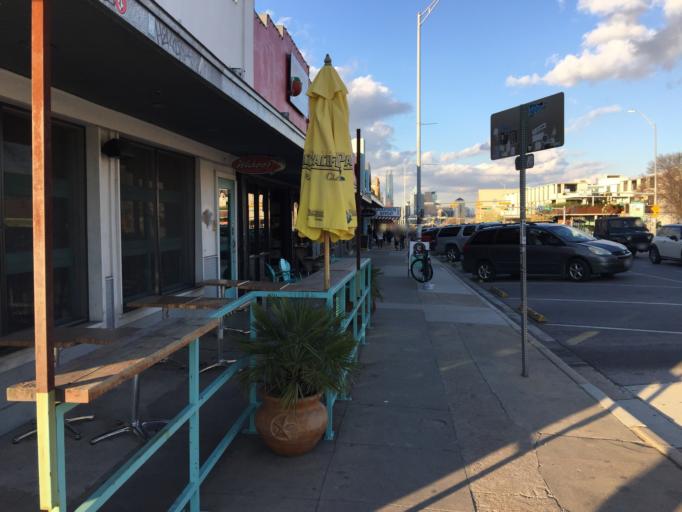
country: US
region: Texas
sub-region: Travis County
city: Austin
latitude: 30.2462
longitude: -97.7511
